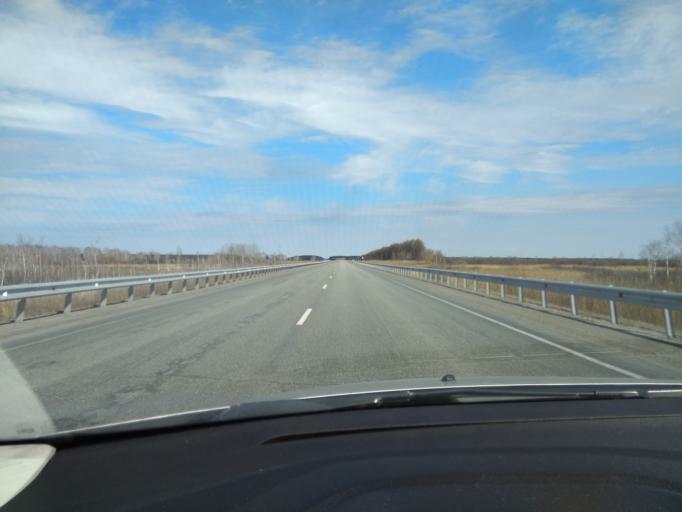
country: RU
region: Sverdlovsk
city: Troitskiy
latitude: 57.0860
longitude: 63.7078
